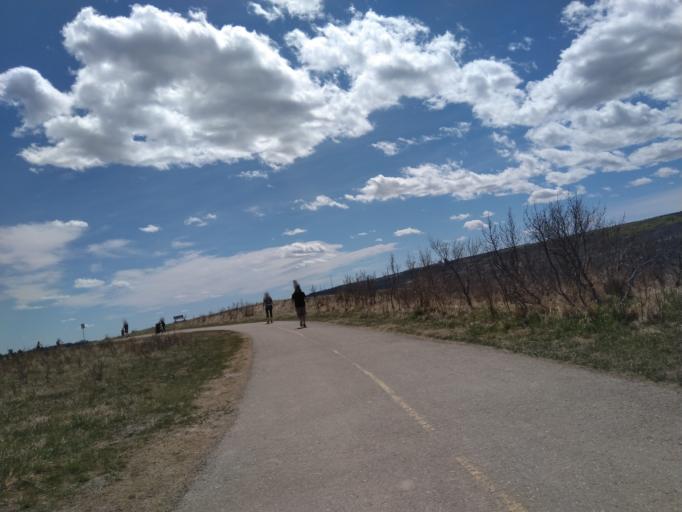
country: CA
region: Alberta
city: Calgary
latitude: 51.1017
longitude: -114.1970
